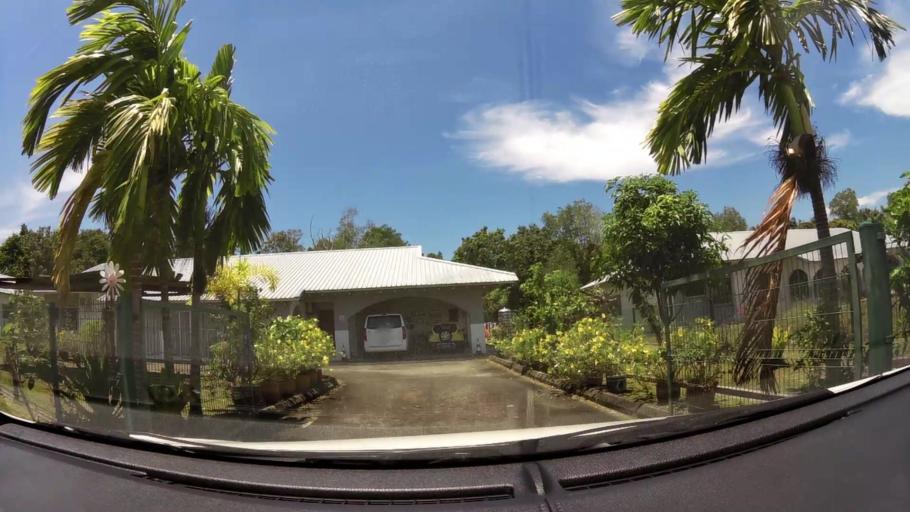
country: BN
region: Brunei and Muara
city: Bandar Seri Begawan
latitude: 4.9221
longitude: 114.9615
